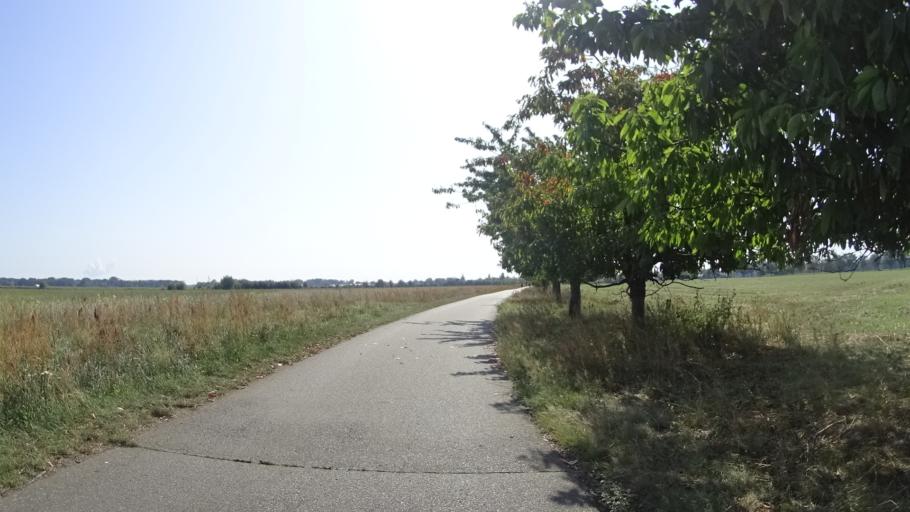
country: DE
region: Brandenburg
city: Werben
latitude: 51.8212
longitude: 14.1661
